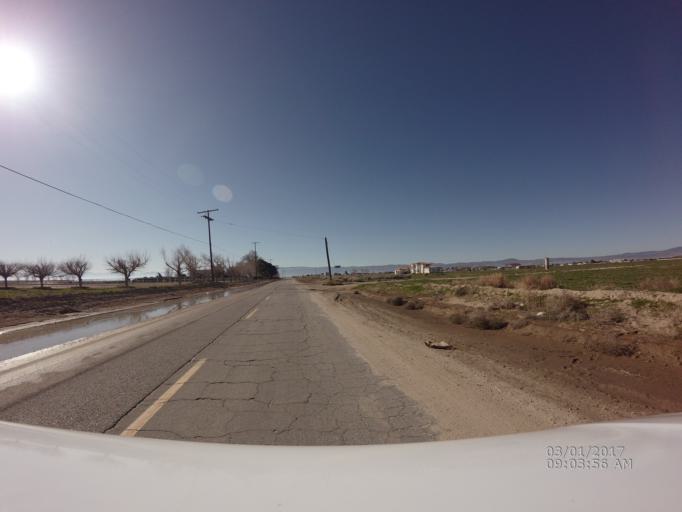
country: US
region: California
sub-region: Los Angeles County
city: Quartz Hill
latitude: 34.7732
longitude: -118.2726
